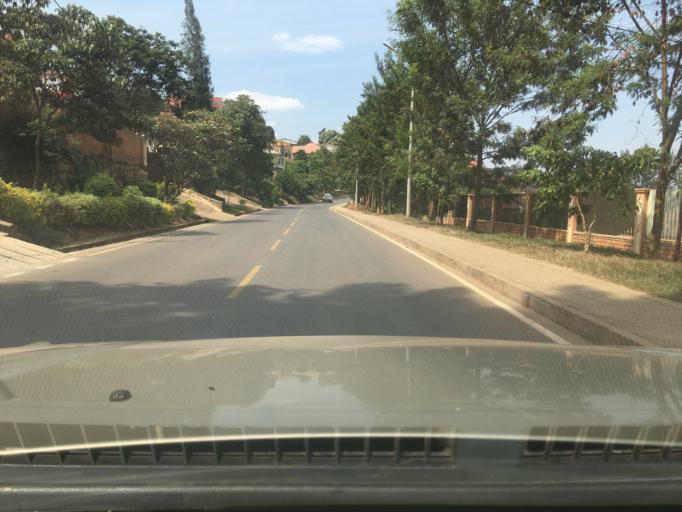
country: RW
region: Kigali
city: Kigali
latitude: -1.9560
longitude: 30.1022
